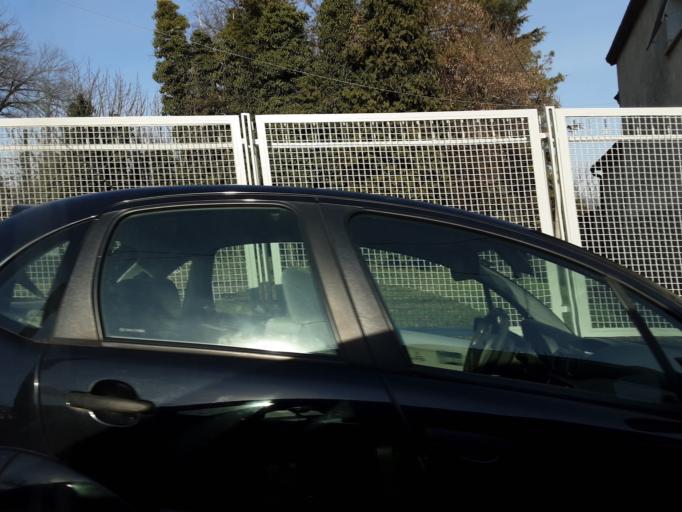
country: IT
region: Veneto
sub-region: Provincia di Treviso
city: Vittorio Veneto
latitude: 45.9698
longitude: 12.2989
